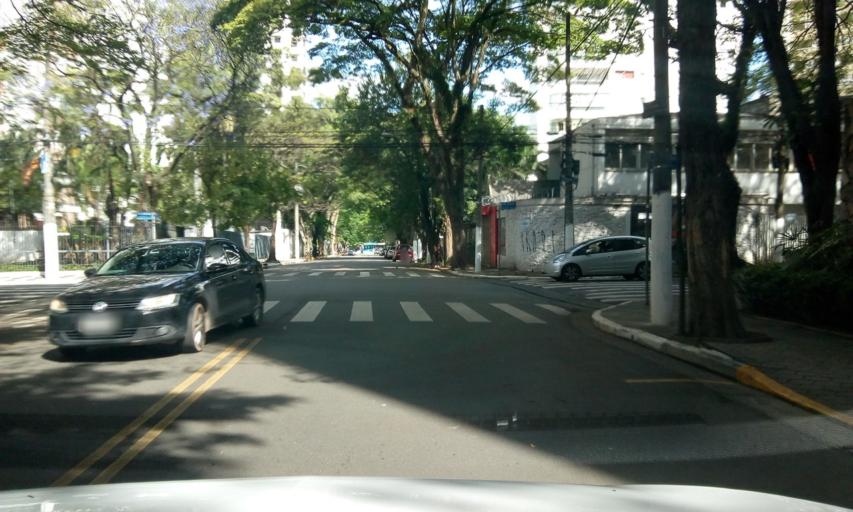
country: BR
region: Sao Paulo
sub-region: Sao Paulo
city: Sao Paulo
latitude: -23.6162
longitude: -46.6775
